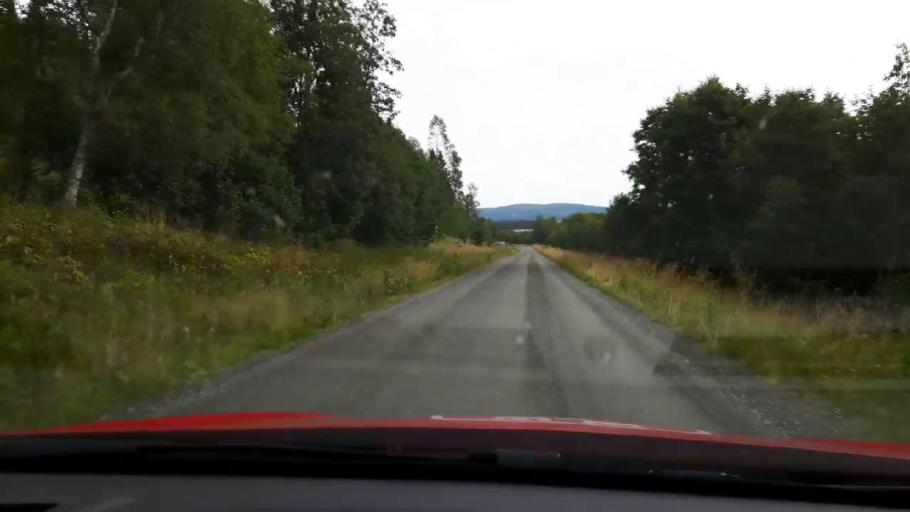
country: SE
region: Jaemtland
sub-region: Are Kommun
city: Are
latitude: 63.7464
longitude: 12.9721
